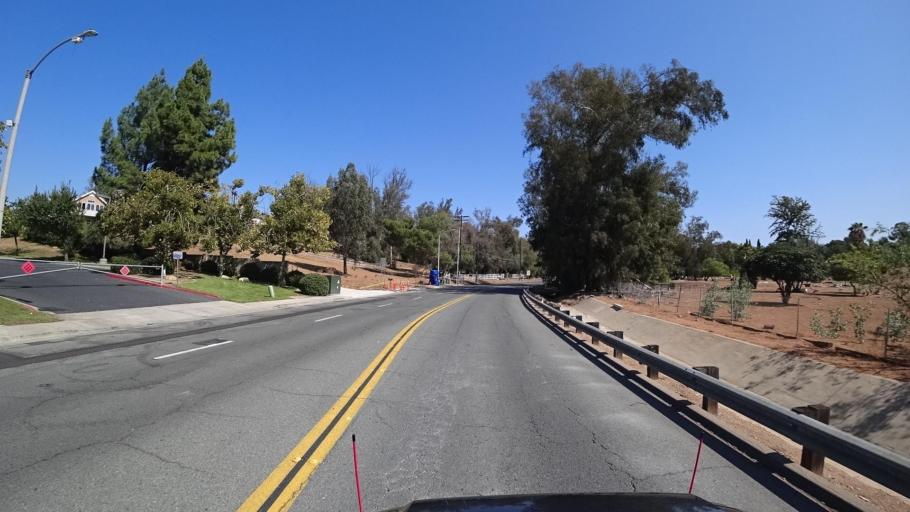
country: US
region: California
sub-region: San Diego County
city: Granite Hills
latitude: 32.7876
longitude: -116.9171
